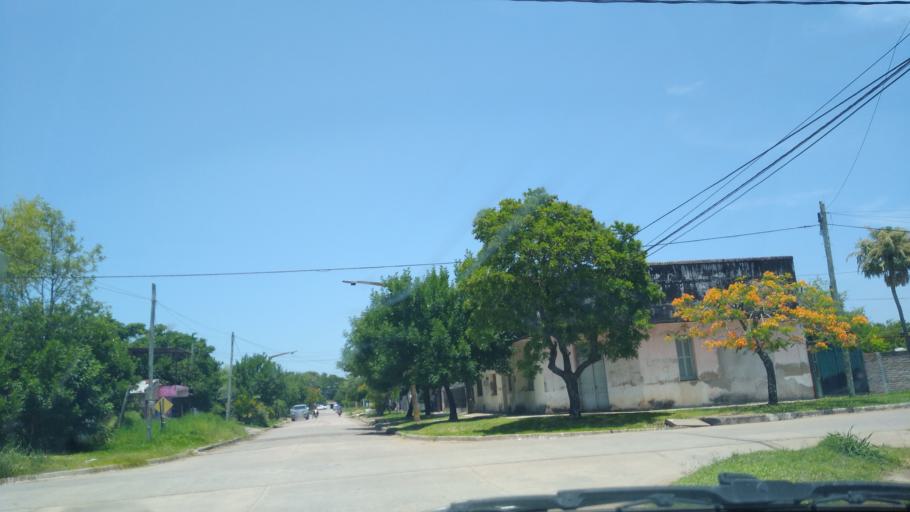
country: AR
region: Chaco
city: Barranqueras
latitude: -27.4891
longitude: -58.9395
